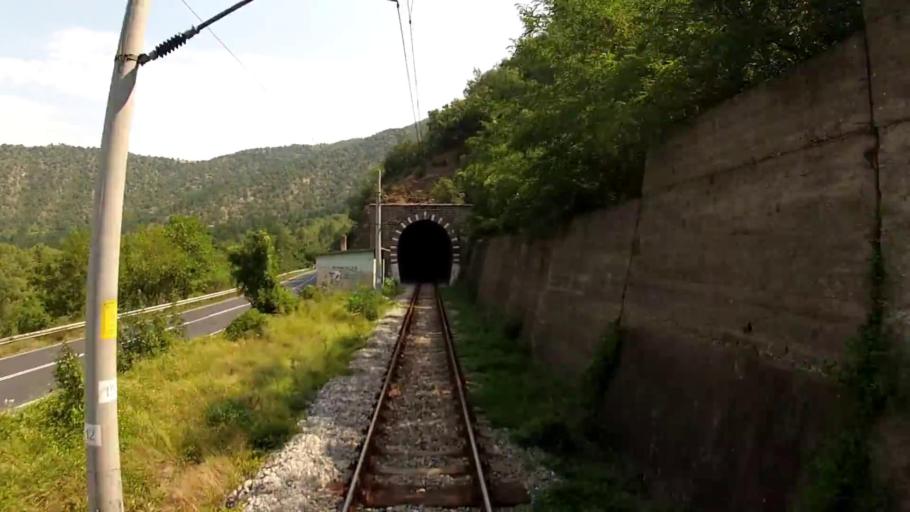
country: BG
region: Blagoevgrad
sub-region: Obshtina Kresna
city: Kresna
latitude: 41.7228
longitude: 23.1562
